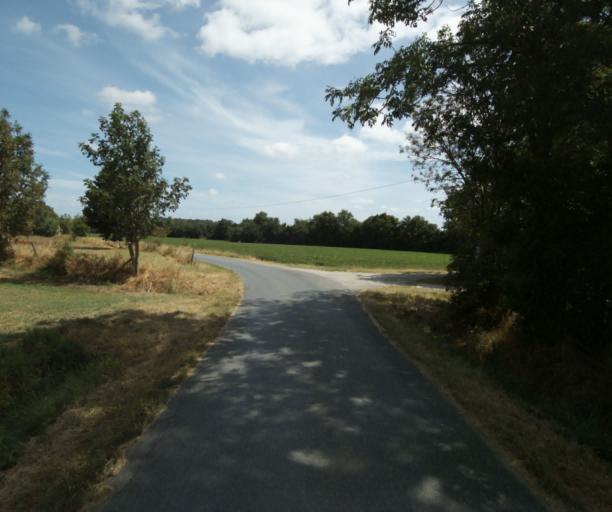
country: FR
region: Midi-Pyrenees
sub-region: Departement du Tarn
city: Soreze
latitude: 43.4943
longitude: 2.0821
